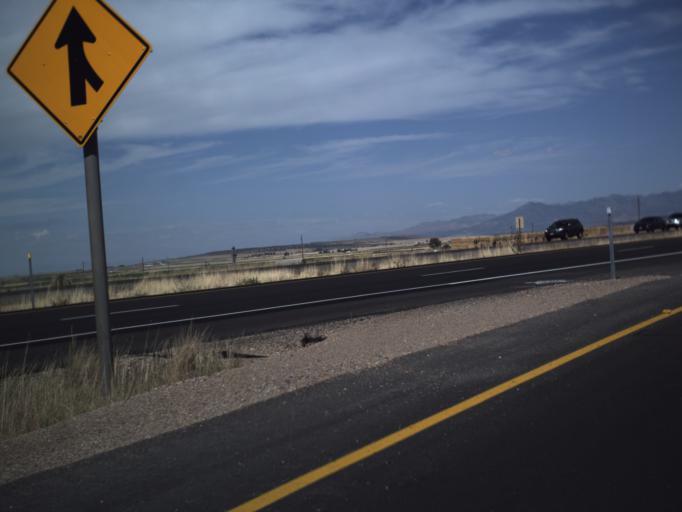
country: US
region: Utah
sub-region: Millard County
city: Fillmore
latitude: 38.8946
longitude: -112.4101
